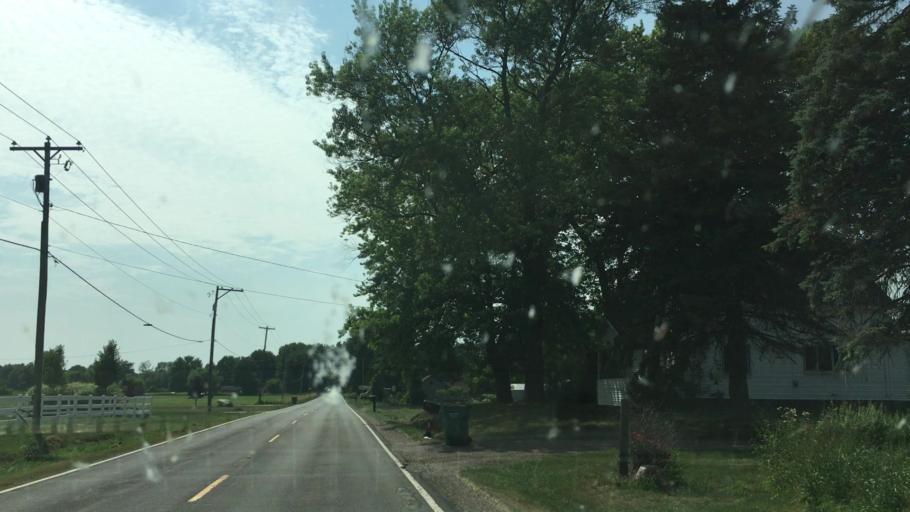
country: US
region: Michigan
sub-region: Kent County
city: Byron Center
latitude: 42.7828
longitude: -85.7082
